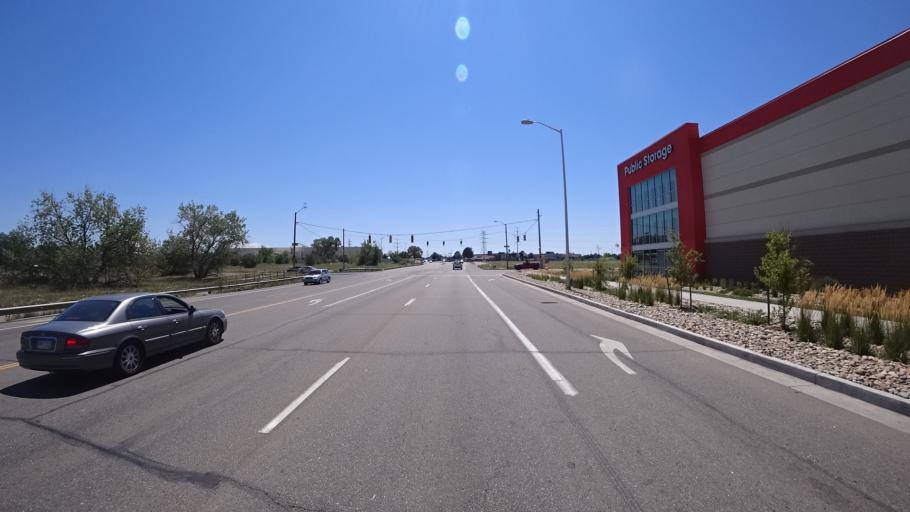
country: US
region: Colorado
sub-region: El Paso County
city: Stratmoor
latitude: 38.7911
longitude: -104.7634
